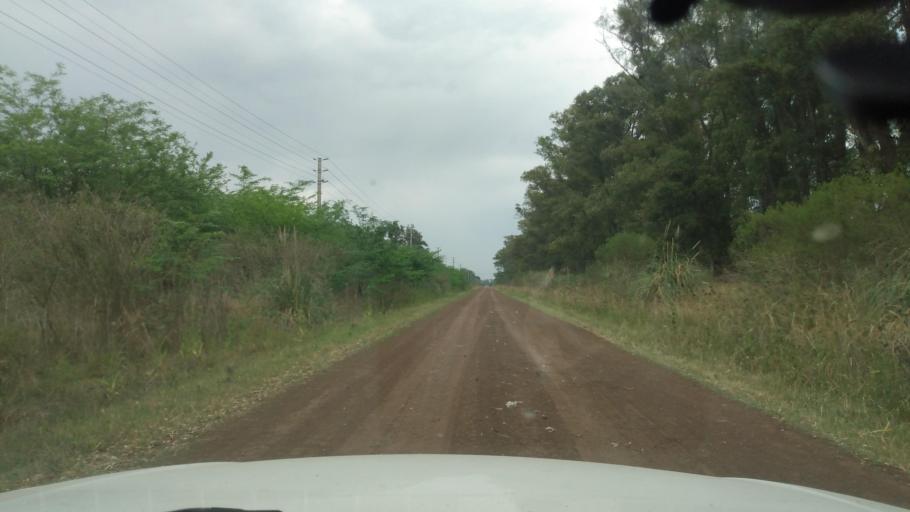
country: AR
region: Buenos Aires
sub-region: Partido de Lujan
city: Lujan
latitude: -34.5518
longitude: -59.1708
